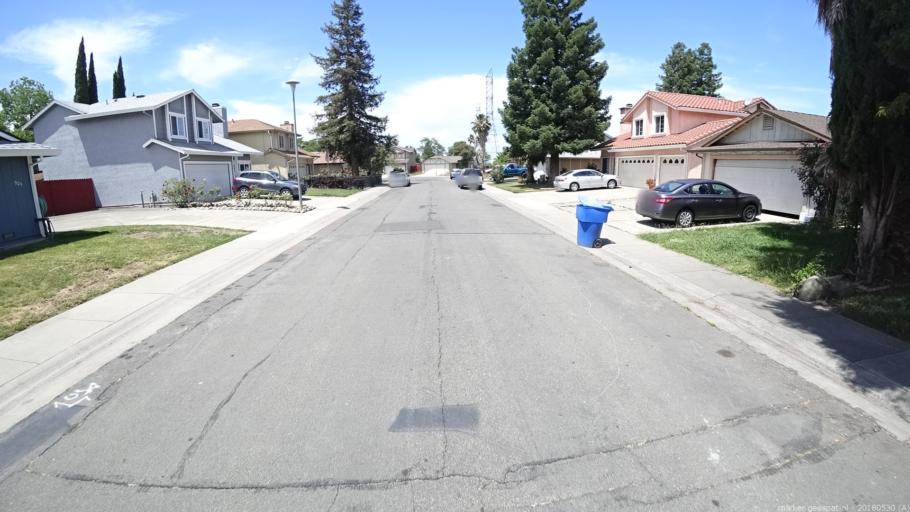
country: US
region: California
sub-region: Sacramento County
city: Sacramento
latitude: 38.6344
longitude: -121.4827
